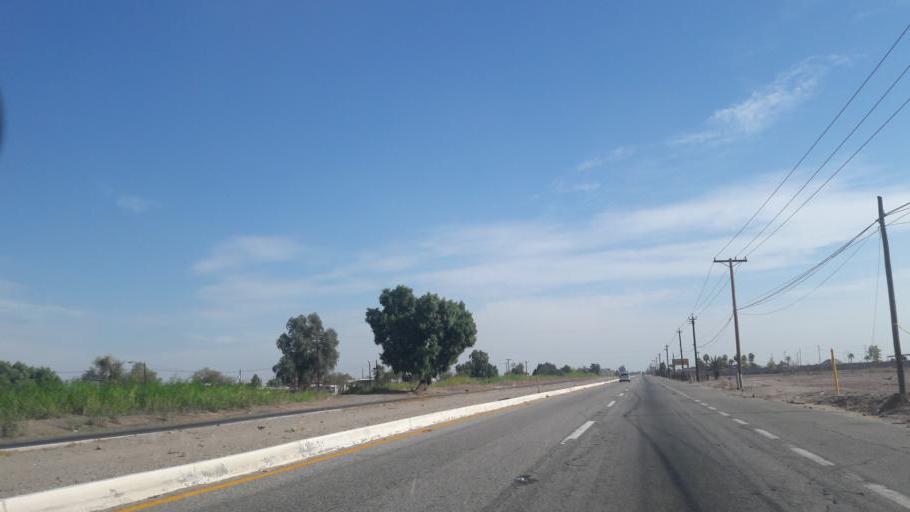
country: MX
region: Baja California
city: Progreso
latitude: 32.5926
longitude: -115.6226
